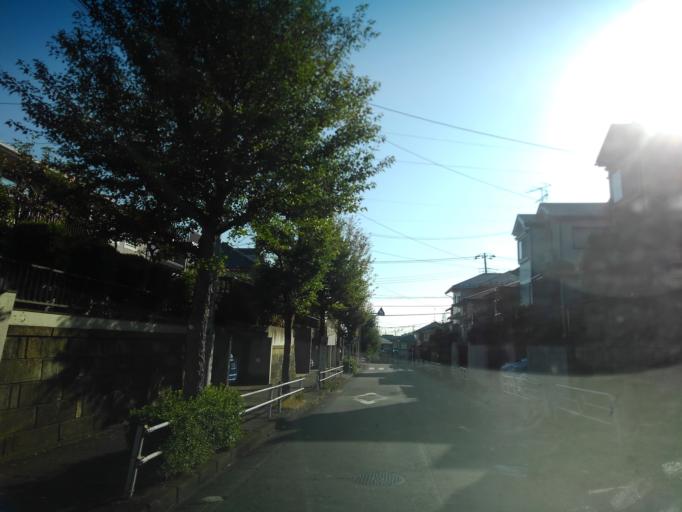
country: JP
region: Tokyo
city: Hachioji
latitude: 35.6891
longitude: 139.3507
